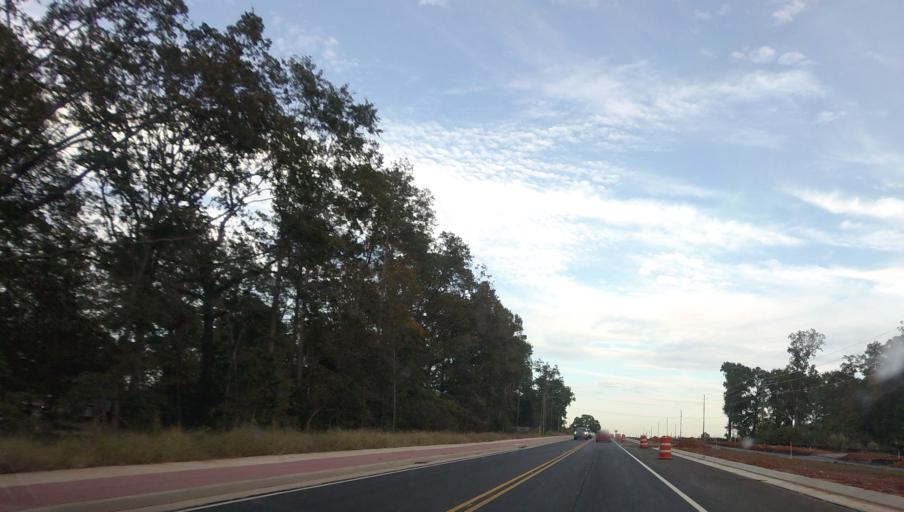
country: US
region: Georgia
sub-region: Houston County
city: Centerville
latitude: 32.5546
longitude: -83.6830
